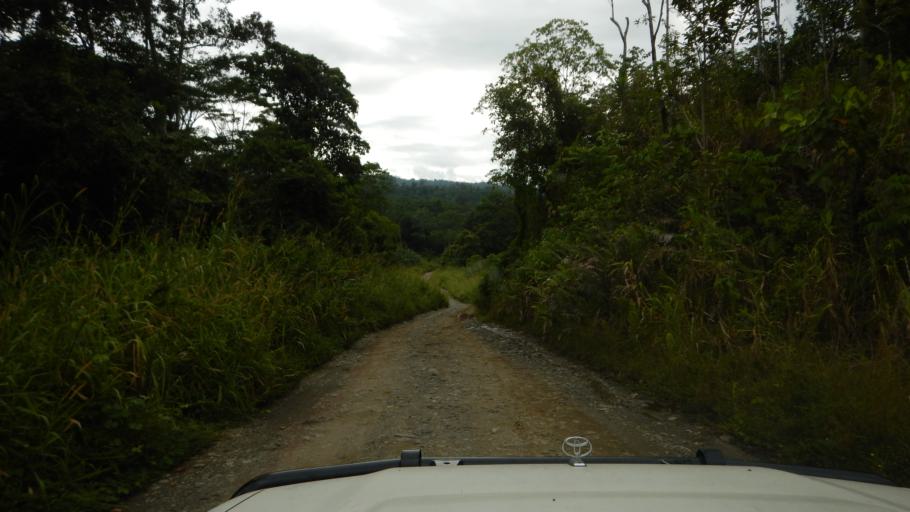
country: PG
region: Northern Province
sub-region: Sohe
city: Kokoda
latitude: -8.9169
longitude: 147.8505
